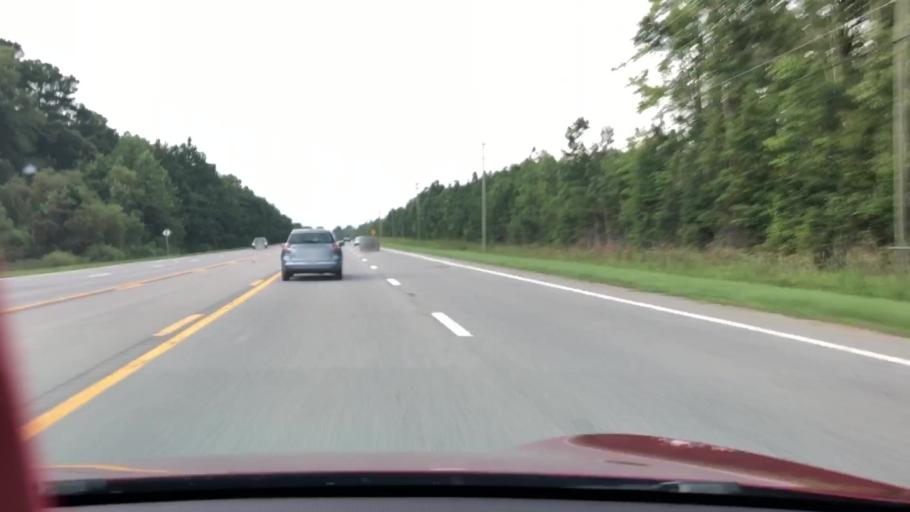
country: US
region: North Carolina
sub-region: Currituck County
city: Moyock
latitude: 36.4824
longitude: -76.1321
